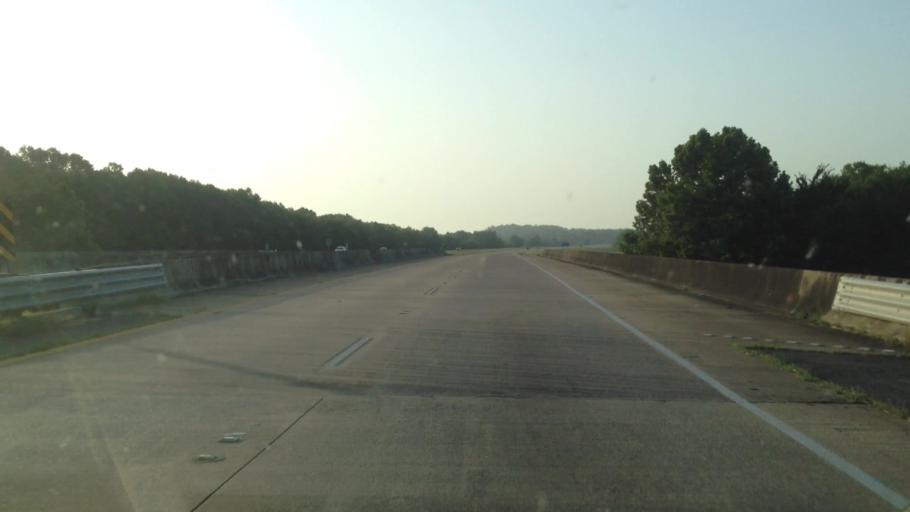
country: US
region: Louisiana
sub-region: Grant Parish
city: Colfax
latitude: 31.5023
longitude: -92.8751
